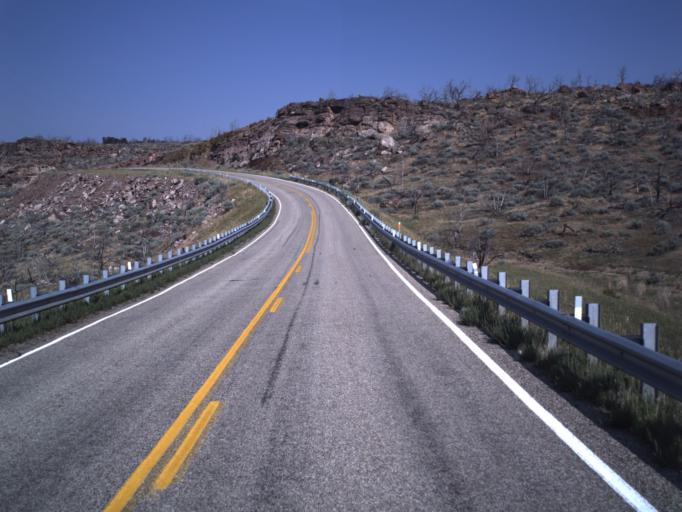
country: US
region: Utah
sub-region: Daggett County
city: Manila
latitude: 40.9414
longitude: -109.4138
